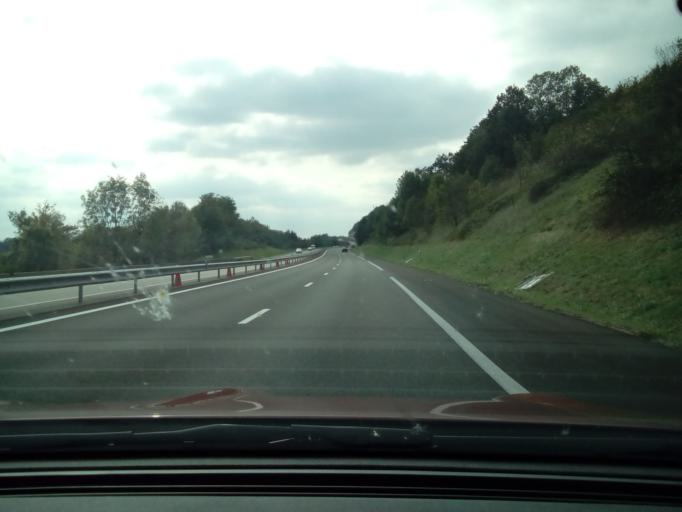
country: FR
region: Rhone-Alpes
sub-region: Departement de l'Isere
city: Vinay
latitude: 45.1755
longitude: 5.3905
